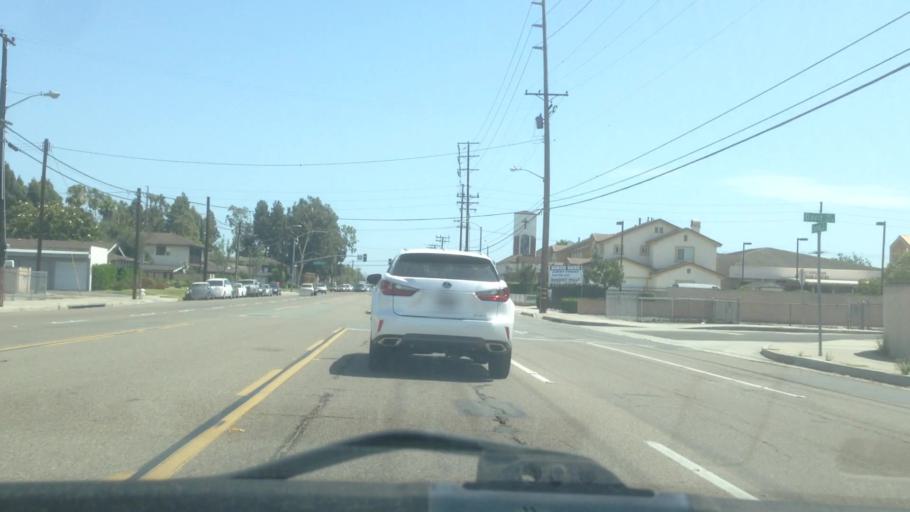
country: US
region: California
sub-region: Orange County
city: Garden Grove
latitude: 33.7398
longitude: -117.9374
